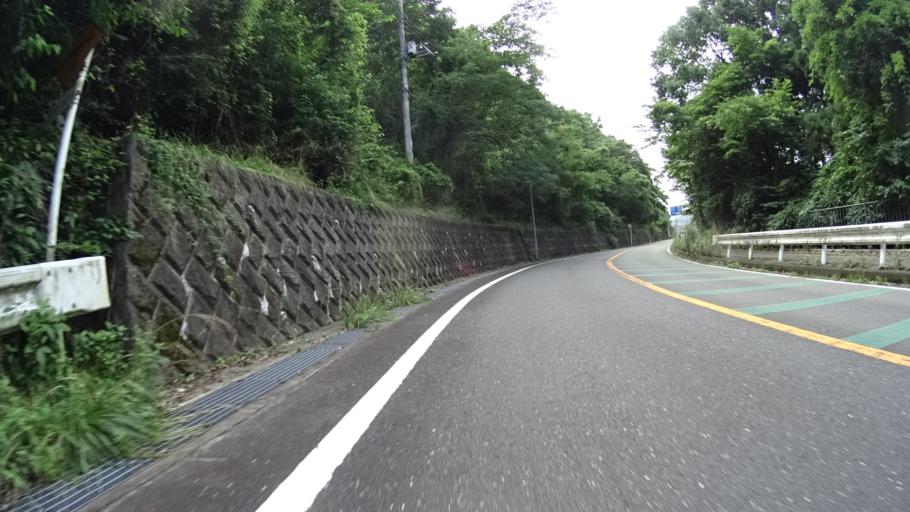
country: JP
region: Kanagawa
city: Hadano
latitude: 35.5173
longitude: 139.2313
